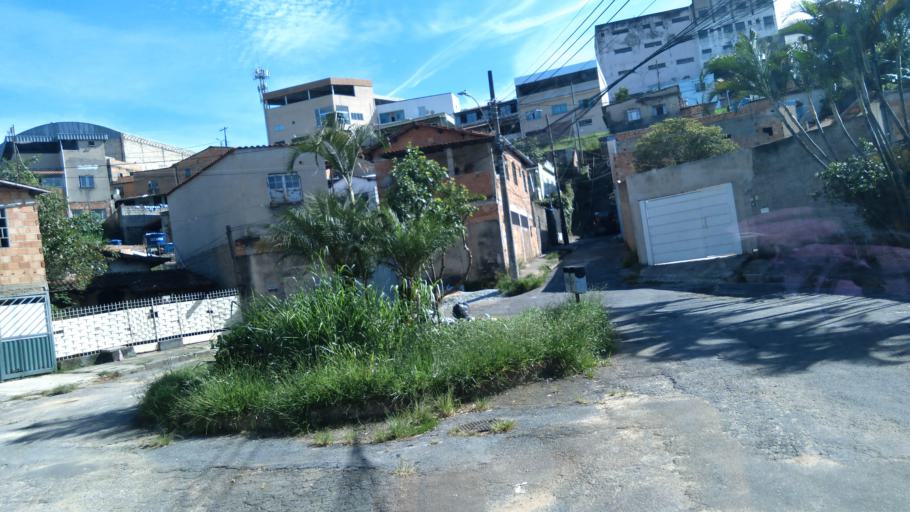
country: BR
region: Minas Gerais
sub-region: Contagem
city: Contagem
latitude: -19.9059
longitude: -44.0026
